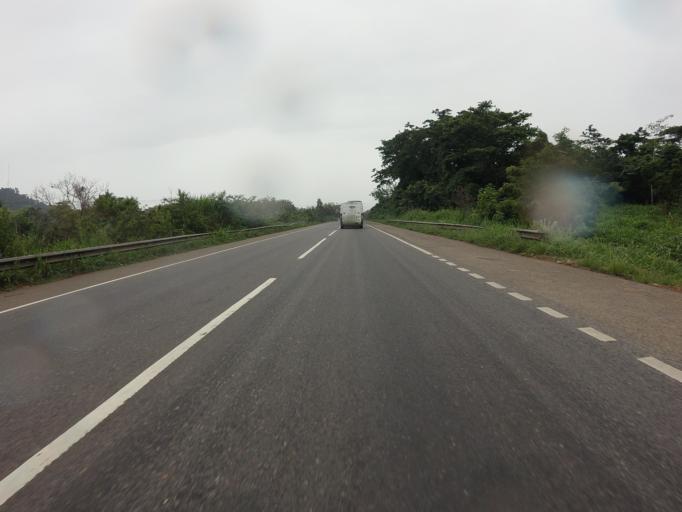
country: GH
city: Kibi
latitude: 6.1337
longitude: -0.4946
